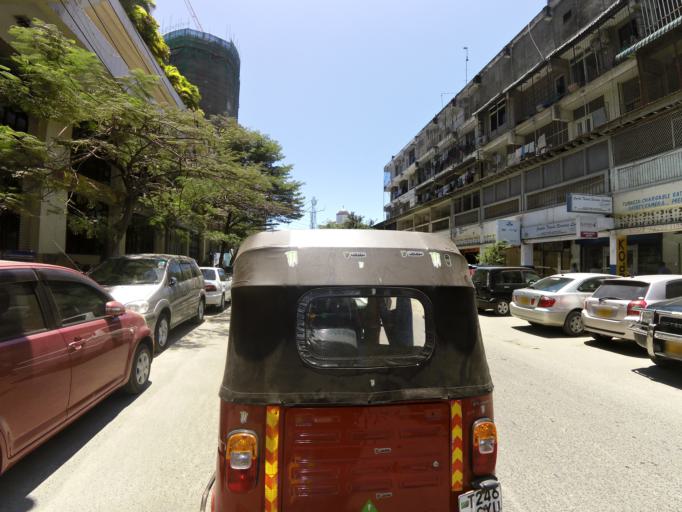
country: TZ
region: Dar es Salaam
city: Dar es Salaam
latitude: -6.8150
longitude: 39.2867
